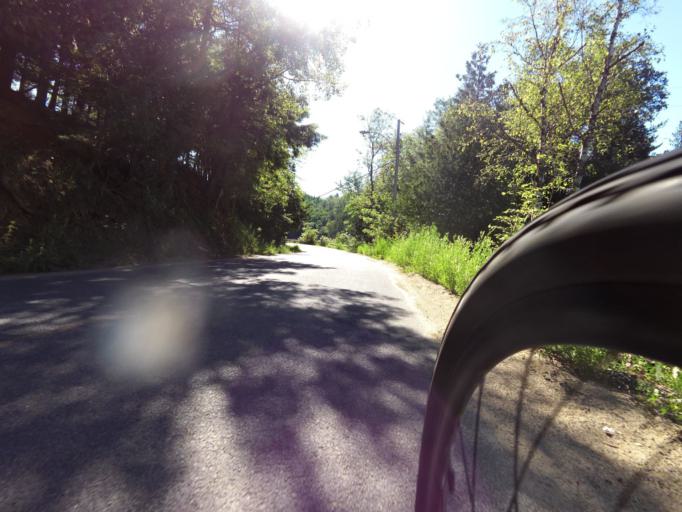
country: CA
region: Quebec
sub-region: Laurentides
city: Brownsburg-Chatham
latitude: 45.9040
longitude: -74.5978
